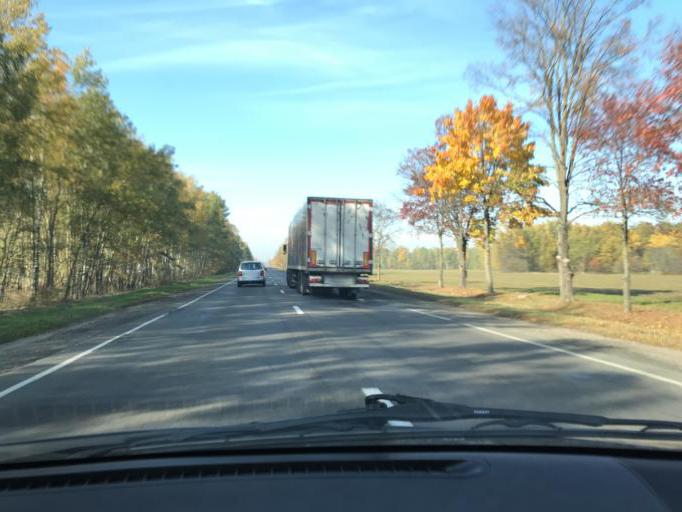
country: BY
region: Brest
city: Luninyets
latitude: 52.2747
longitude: 26.8906
